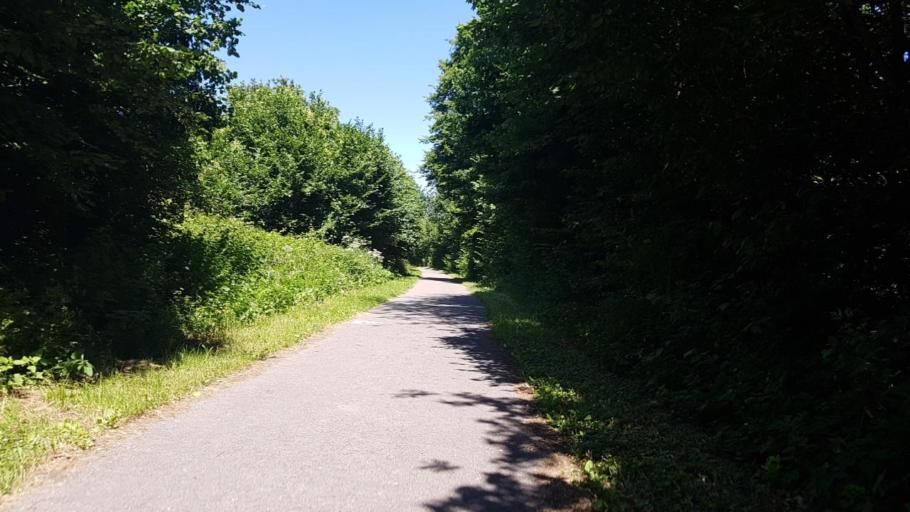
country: BE
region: Wallonia
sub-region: Province du Hainaut
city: Beaumont
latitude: 50.2244
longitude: 4.2442
